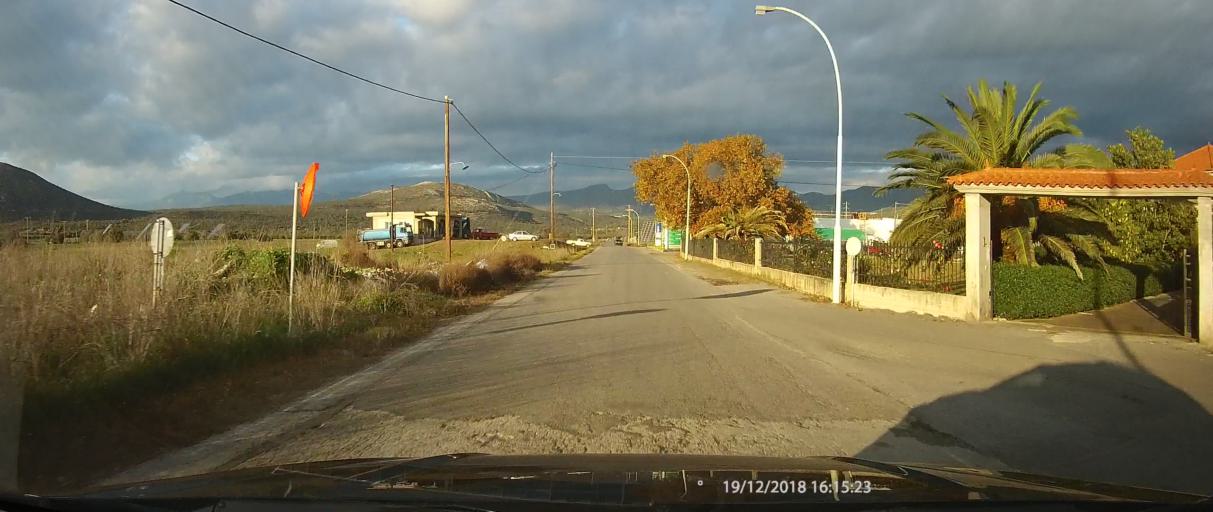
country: GR
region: Peloponnese
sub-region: Nomos Lakonias
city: Kato Glikovrisi
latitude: 36.8894
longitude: 22.8008
